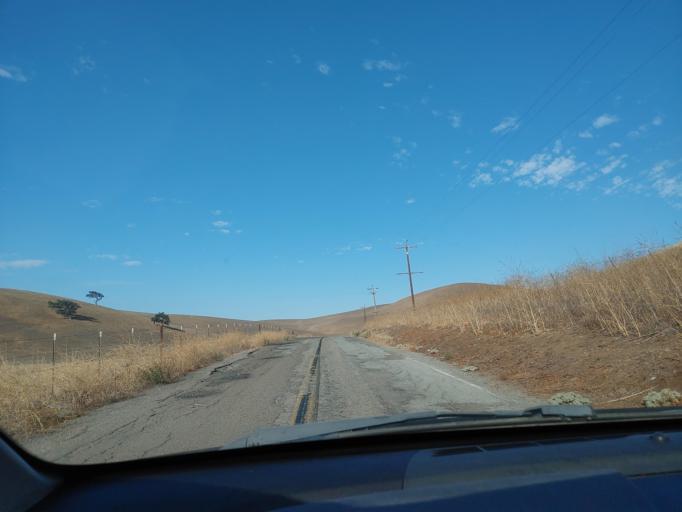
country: US
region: California
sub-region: San Benito County
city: Ridgemark
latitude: 36.7993
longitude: -121.2808
